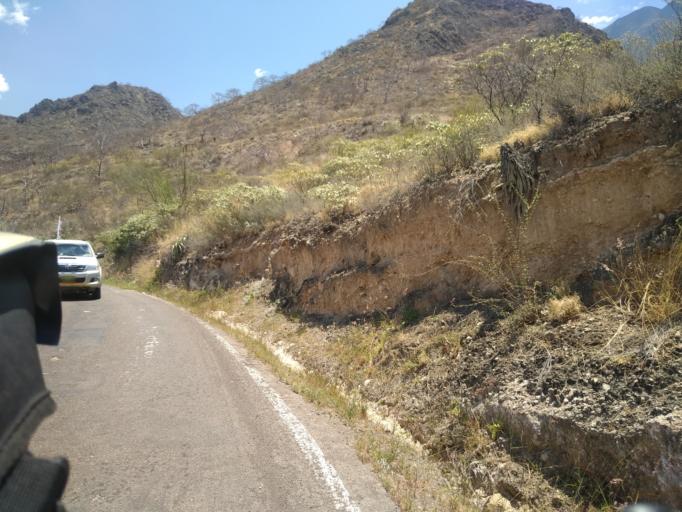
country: PE
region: Amazonas
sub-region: Provincia de Chachapoyas
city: Balsas
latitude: -6.8466
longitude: -78.0429
